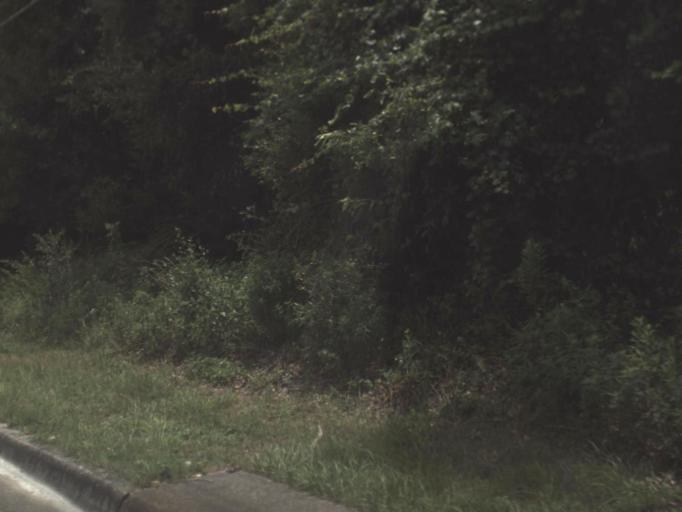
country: US
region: Florida
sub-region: Taylor County
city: Perry
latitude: 30.0959
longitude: -83.5466
